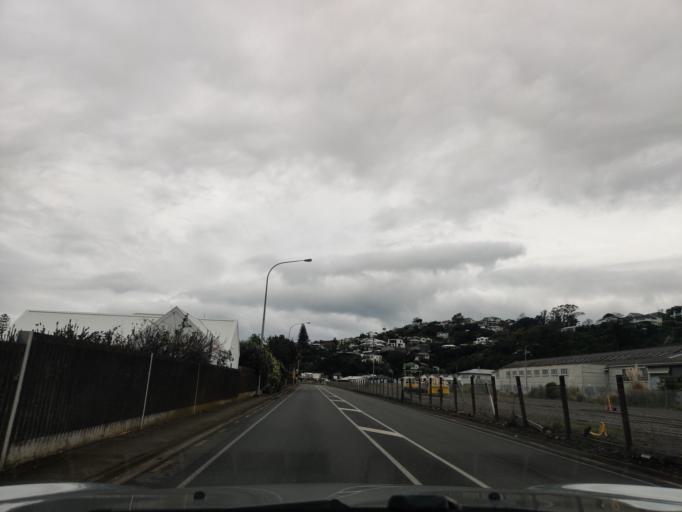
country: NZ
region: Hawke's Bay
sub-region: Napier City
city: Napier
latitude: -39.4797
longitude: 176.9045
